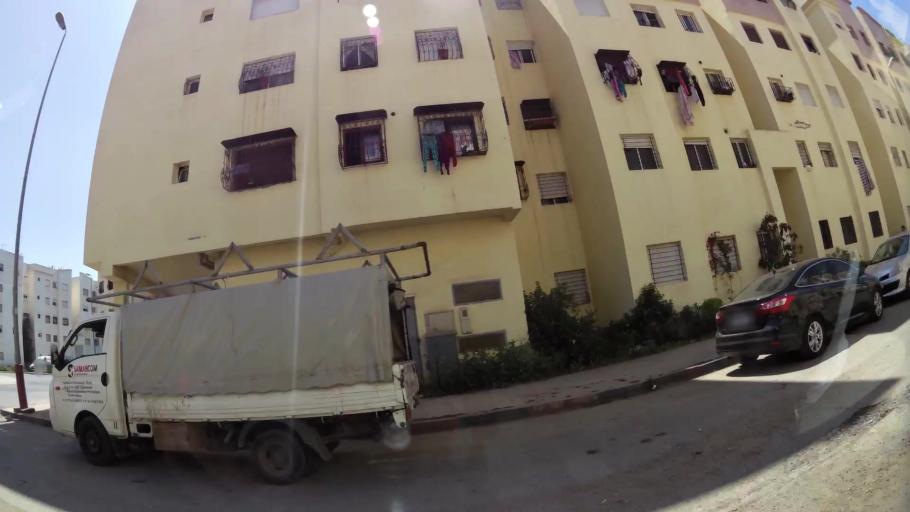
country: MA
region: Rabat-Sale-Zemmour-Zaer
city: Sale
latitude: 34.0815
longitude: -6.7829
